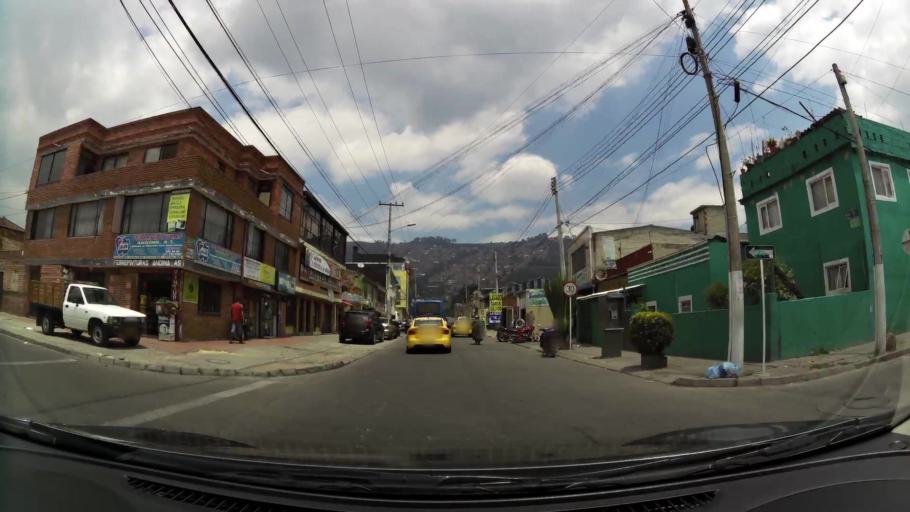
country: CO
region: Cundinamarca
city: La Calera
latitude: 4.7377
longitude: -74.0300
